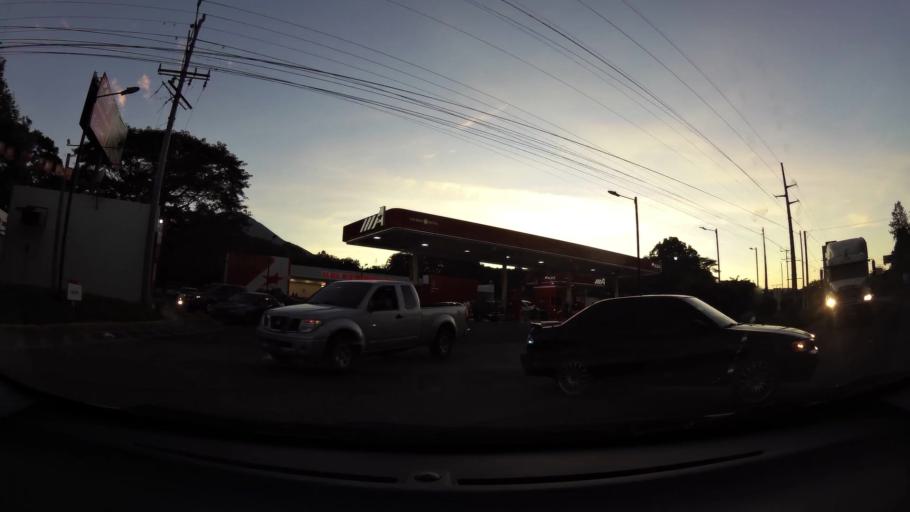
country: SV
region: San Miguel
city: Moncagua
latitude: 13.5062
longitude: -88.2324
